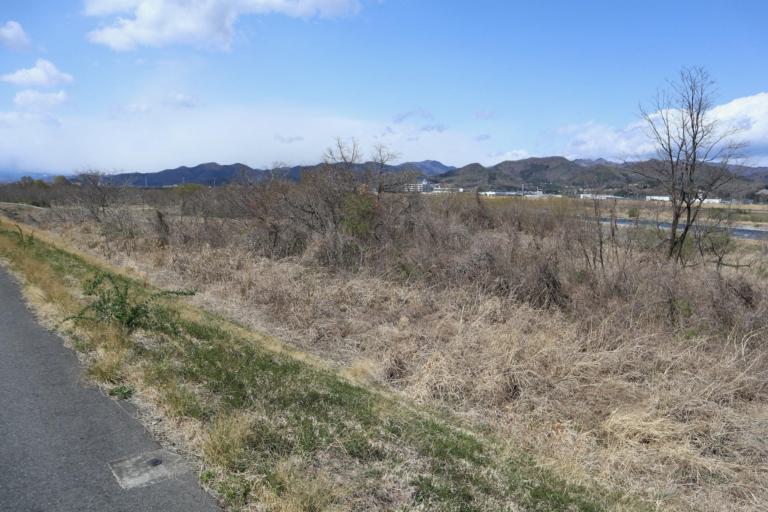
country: JP
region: Gunma
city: Kiryu
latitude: 36.3700
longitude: 139.3620
